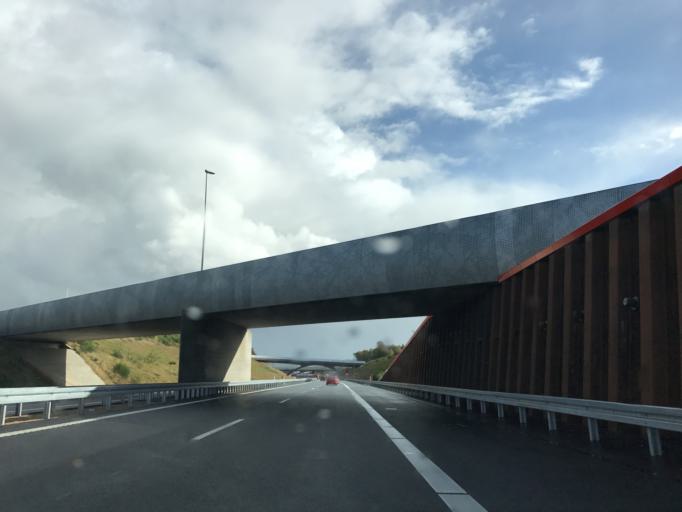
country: DK
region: Central Jutland
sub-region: Silkeborg Kommune
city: Silkeborg
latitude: 56.1957
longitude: 9.5594
